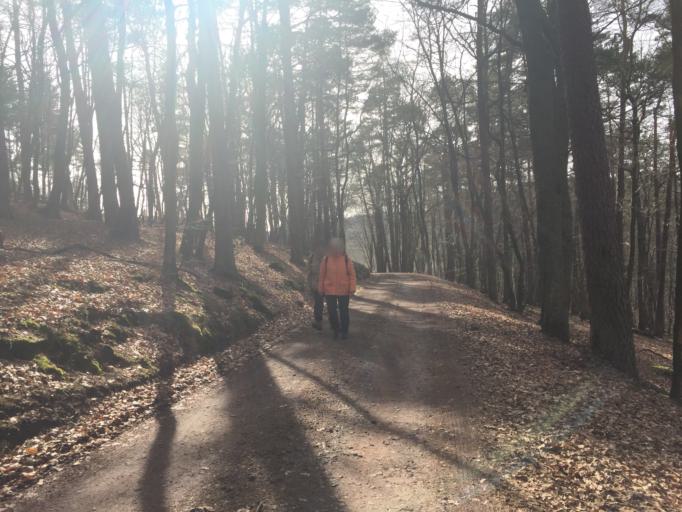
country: DE
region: Rheinland-Pfalz
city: Ramberg
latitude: 49.3001
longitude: 8.0168
